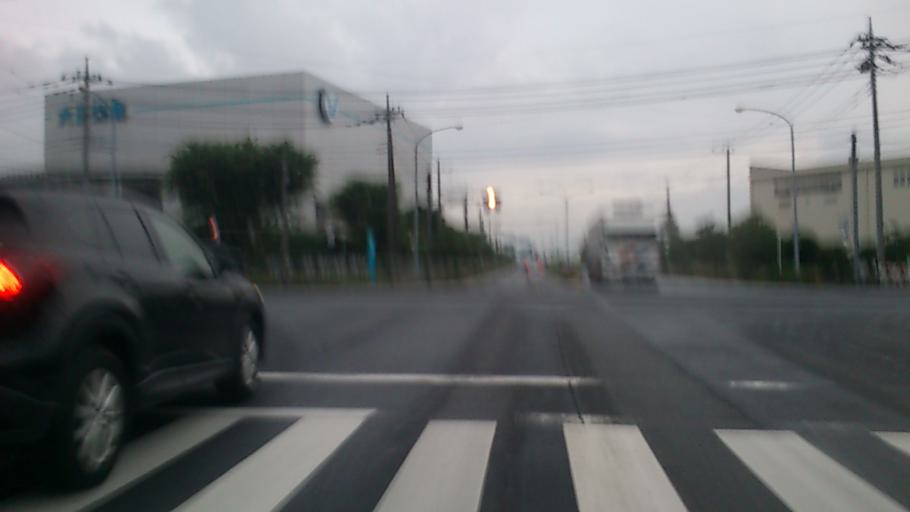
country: JP
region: Saitama
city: Hanyu
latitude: 36.1554
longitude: 139.5347
